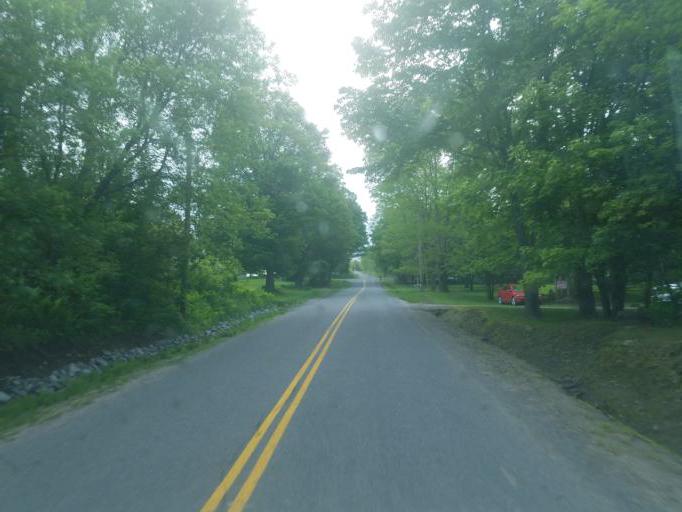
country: US
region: New York
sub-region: Herkimer County
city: Little Falls
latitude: 43.1713
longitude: -74.9336
